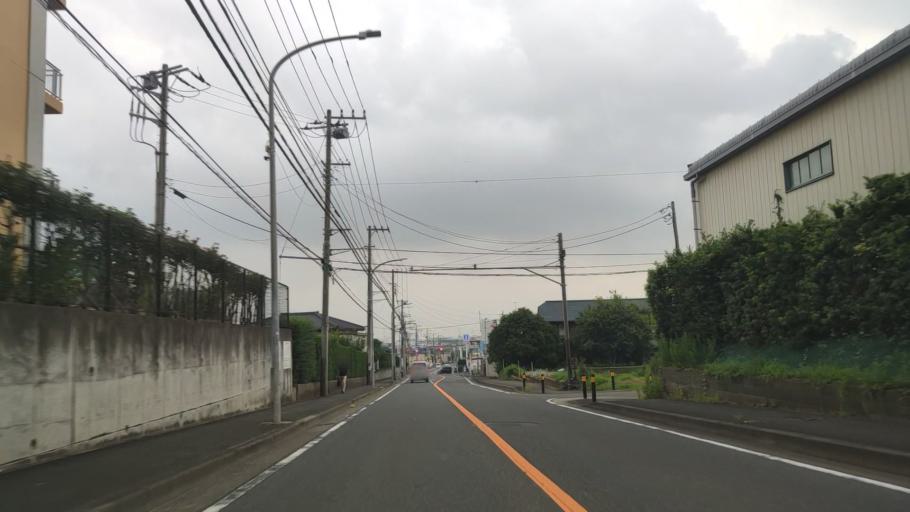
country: JP
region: Kanagawa
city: Minami-rinkan
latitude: 35.4247
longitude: 139.5019
